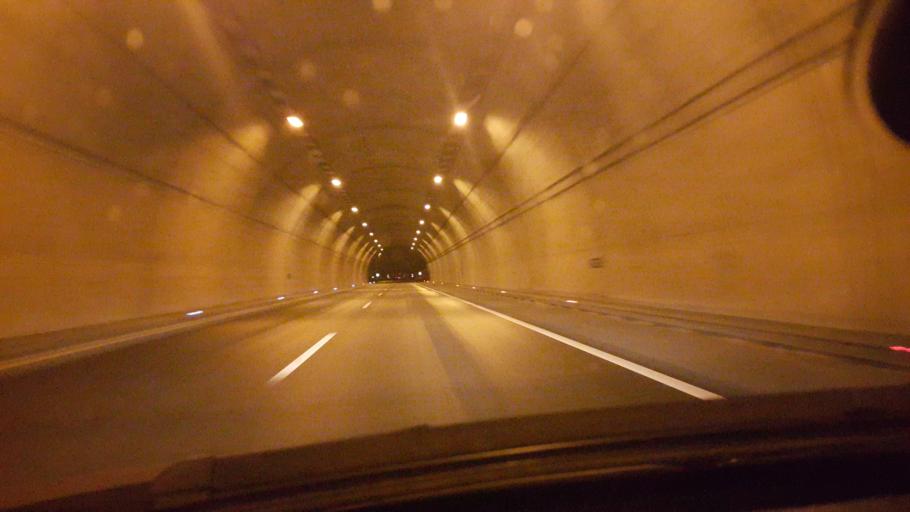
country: SI
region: Maribor
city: Maribor
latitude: 46.5588
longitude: 15.6875
